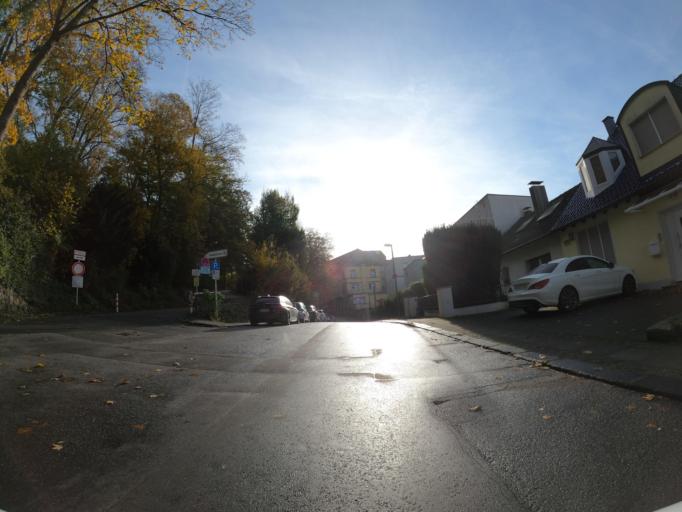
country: DE
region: North Rhine-Westphalia
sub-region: Regierungsbezirk Dusseldorf
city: Wuppertal
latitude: 51.2597
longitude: 7.1564
